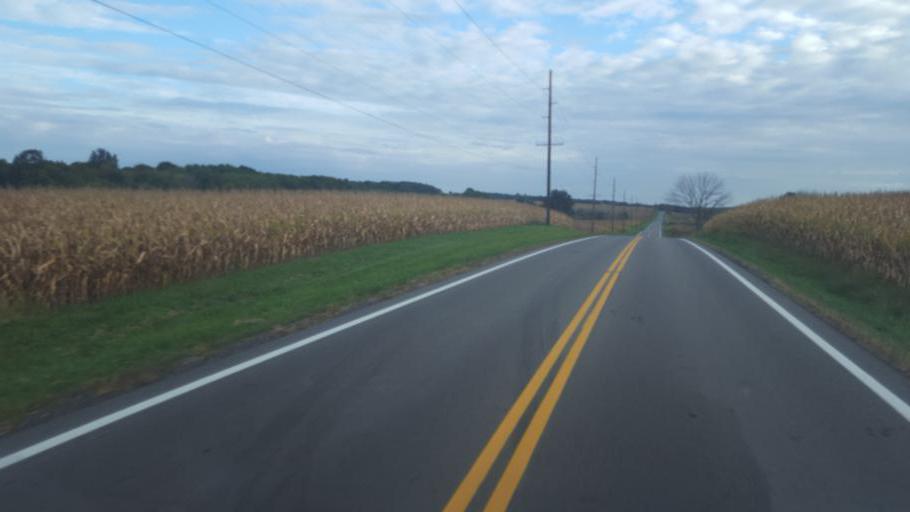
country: US
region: Ohio
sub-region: Ashland County
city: Loudonville
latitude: 40.7493
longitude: -82.1841
